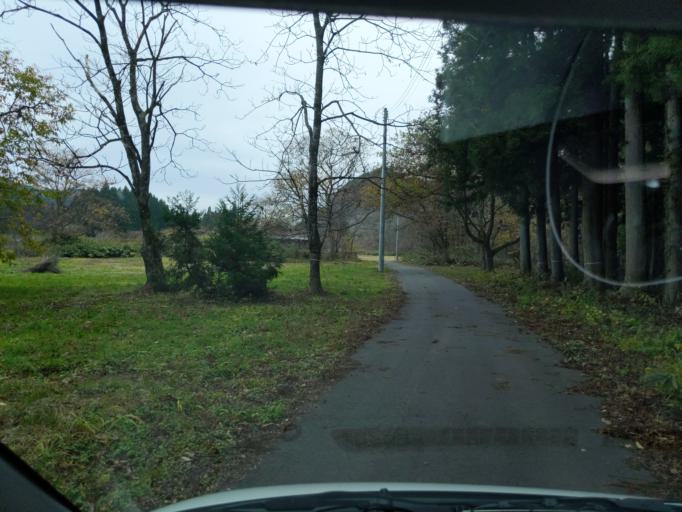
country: JP
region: Iwate
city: Ichinoseki
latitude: 38.9712
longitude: 140.9857
